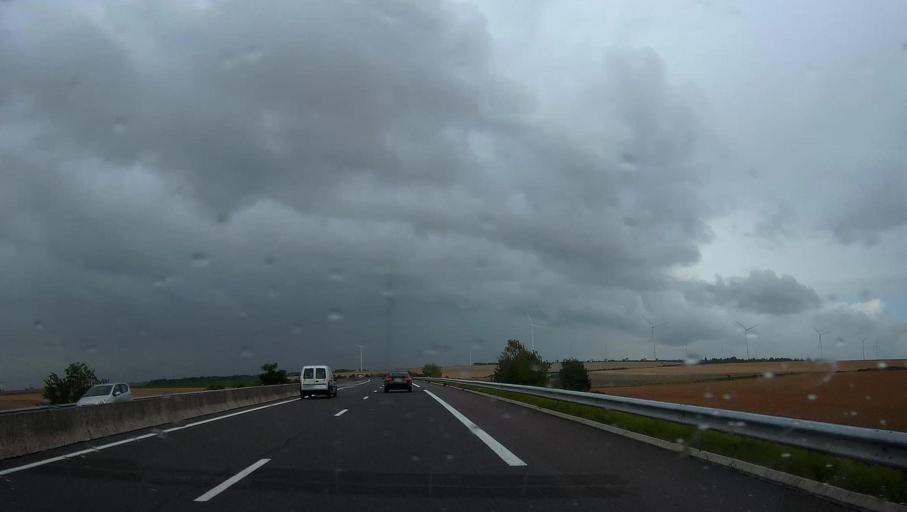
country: FR
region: Champagne-Ardenne
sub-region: Departement de l'Aube
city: Mailly-le-Camp
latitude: 48.6775
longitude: 4.1719
